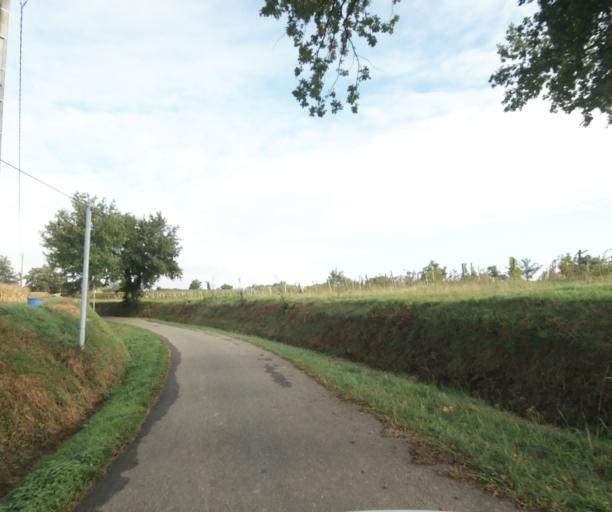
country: FR
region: Midi-Pyrenees
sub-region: Departement du Gers
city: Nogaro
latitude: 43.8103
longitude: -0.0554
